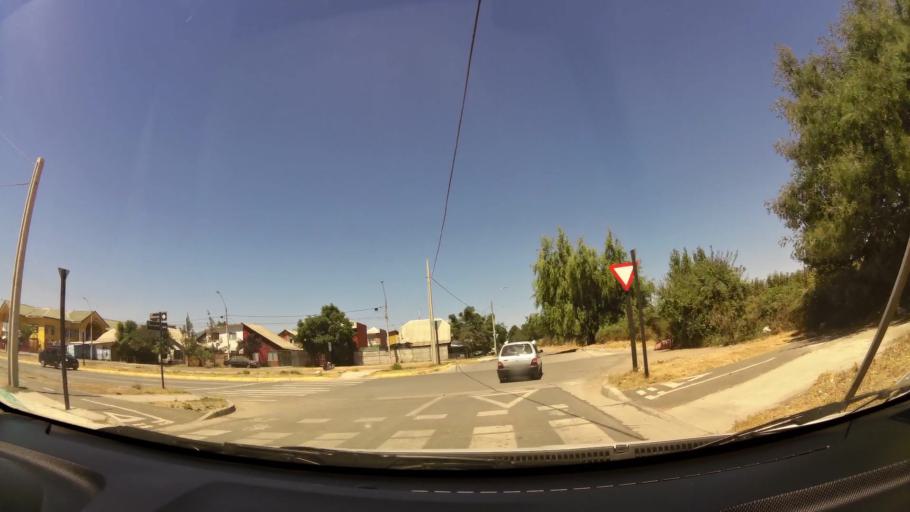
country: CL
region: O'Higgins
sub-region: Provincia de Cachapoal
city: Rancagua
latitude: -34.1526
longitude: -70.7547
